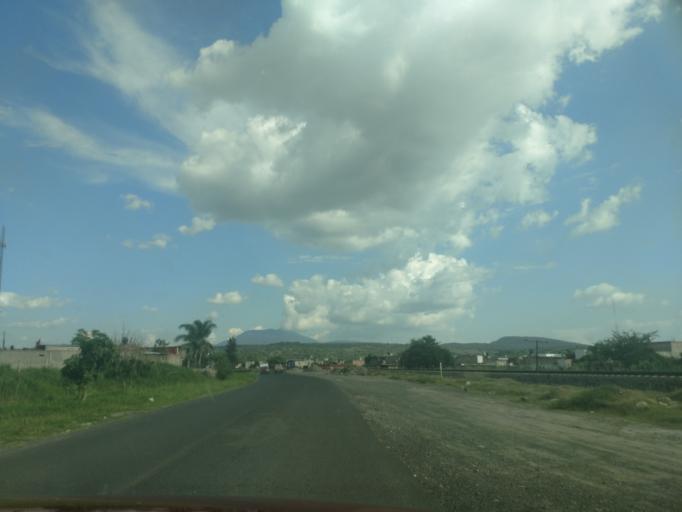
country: MX
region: Jalisco
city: Antonio Escobedo
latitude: 20.9066
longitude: -103.9862
